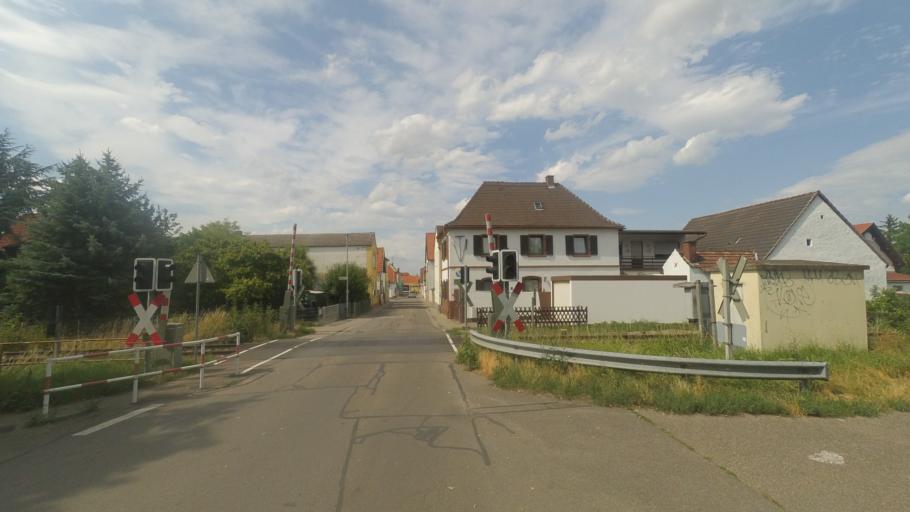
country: DE
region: Rheinland-Pfalz
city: Frankenthal
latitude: 49.5130
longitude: 8.3293
